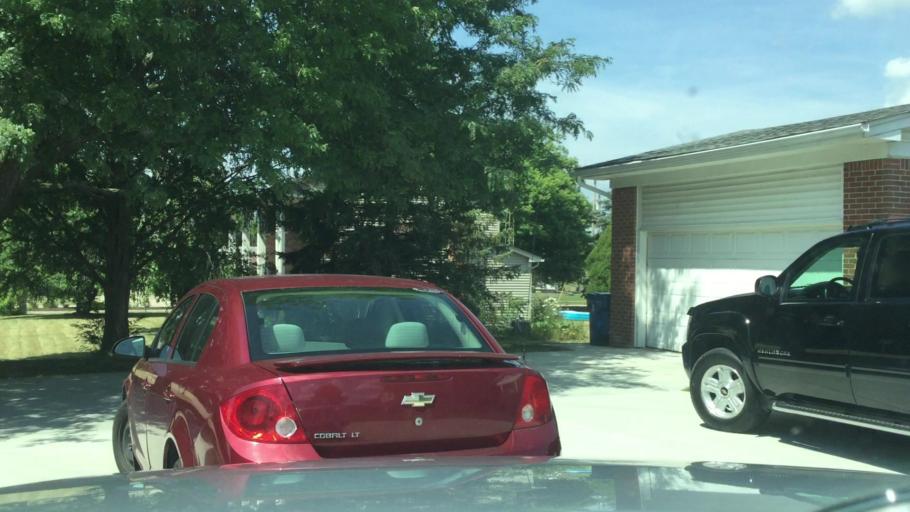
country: US
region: Michigan
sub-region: Genesee County
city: Grand Blanc
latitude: 42.9212
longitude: -83.6400
